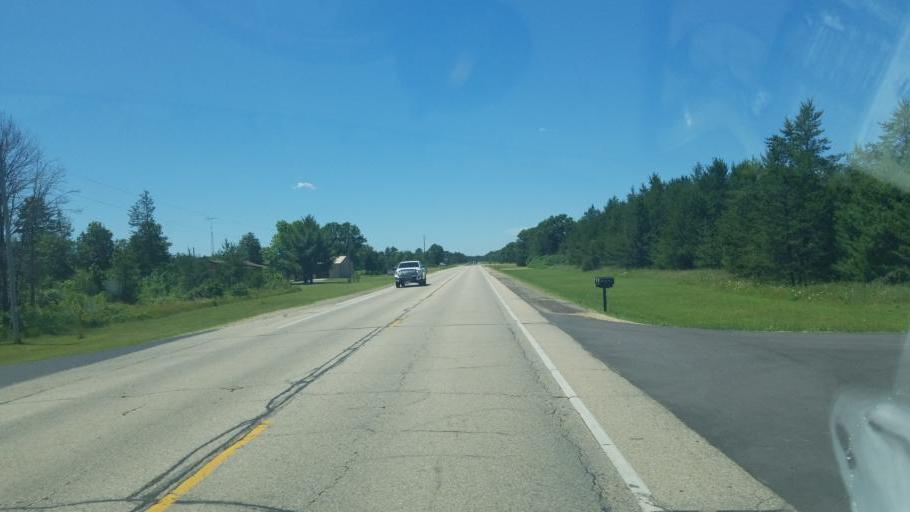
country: US
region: Wisconsin
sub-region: Juneau County
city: New Lisbon
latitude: 44.0405
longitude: -90.0313
